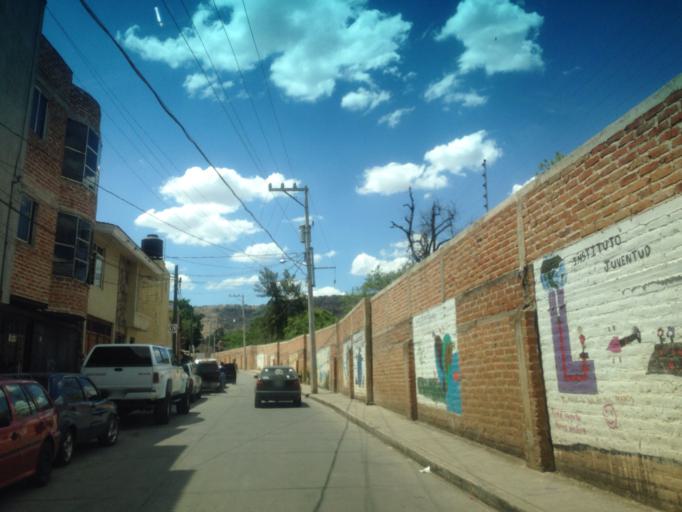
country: MX
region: Jalisco
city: Atotonilco el Alto
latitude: 20.5570
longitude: -102.5110
